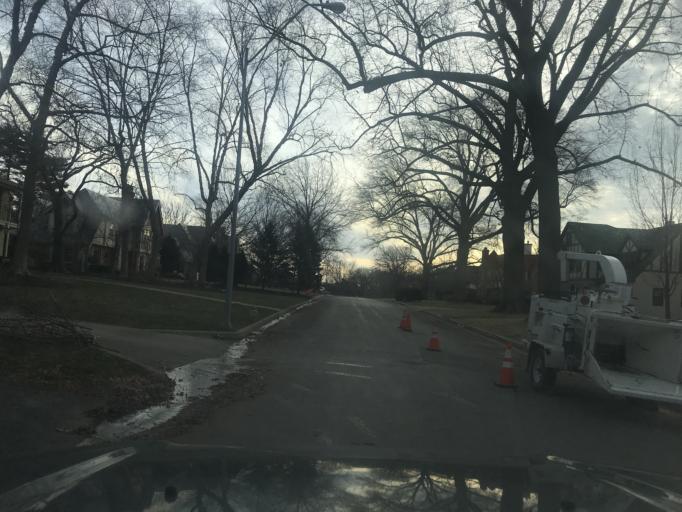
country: US
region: Kansas
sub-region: Johnson County
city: Westwood
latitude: 39.0326
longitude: -94.5989
